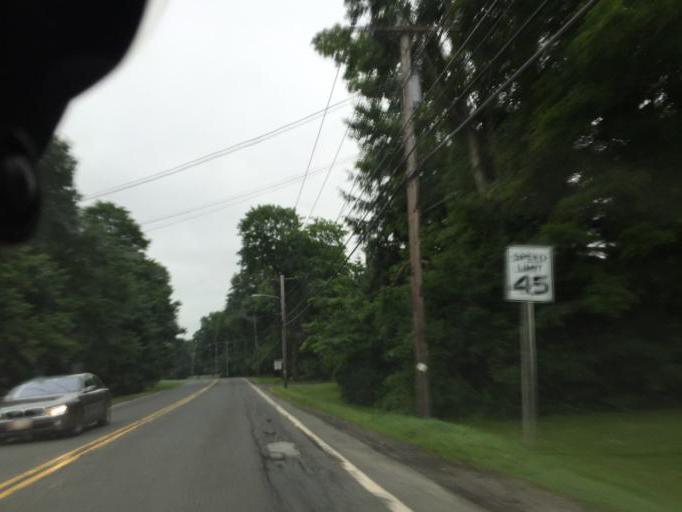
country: US
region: Massachusetts
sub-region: Berkshire County
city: Sheffield
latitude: 42.1032
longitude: -73.3553
